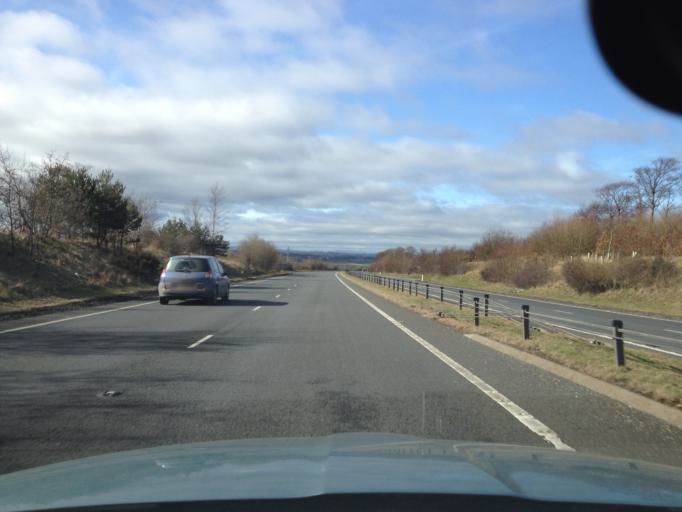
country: GB
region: Scotland
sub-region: East Lothian
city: East Linton
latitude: 55.9769
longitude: -2.6966
